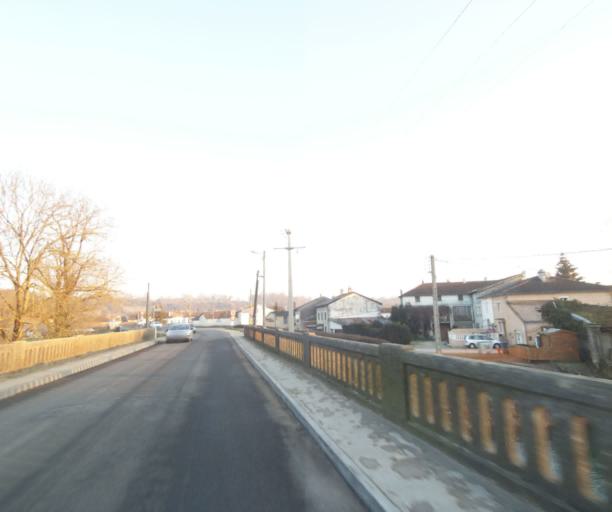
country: FR
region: Champagne-Ardenne
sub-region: Departement de la Haute-Marne
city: Bienville
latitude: 48.6062
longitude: 5.0400
